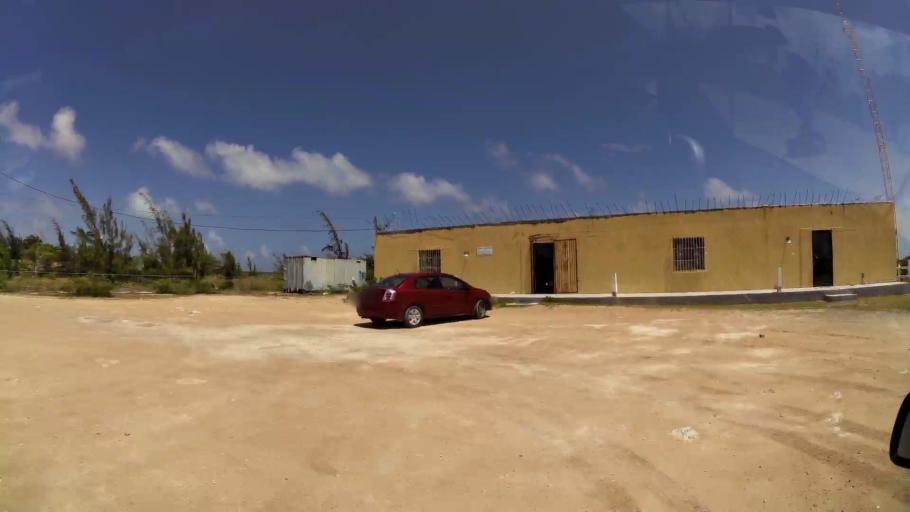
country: TC
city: Cockburn Town
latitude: 21.4487
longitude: -71.1435
